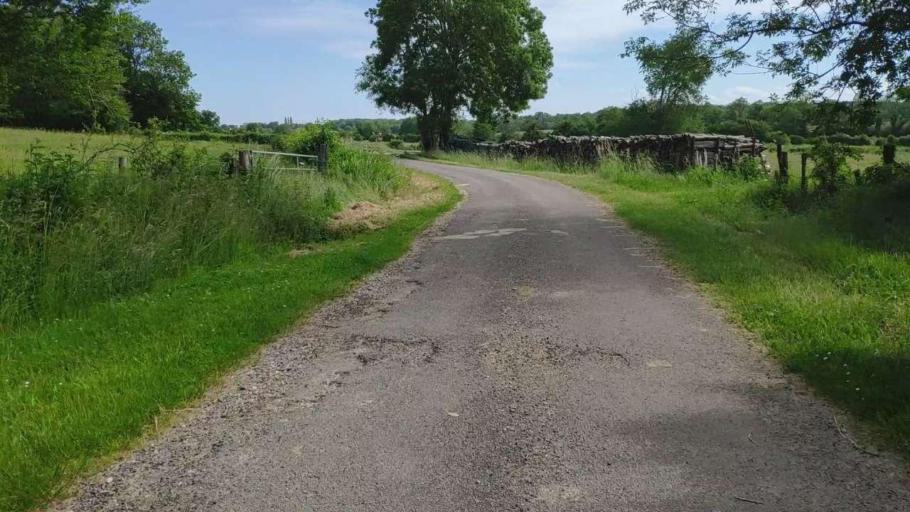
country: FR
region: Franche-Comte
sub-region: Departement du Jura
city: Bletterans
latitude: 46.6857
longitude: 5.4135
